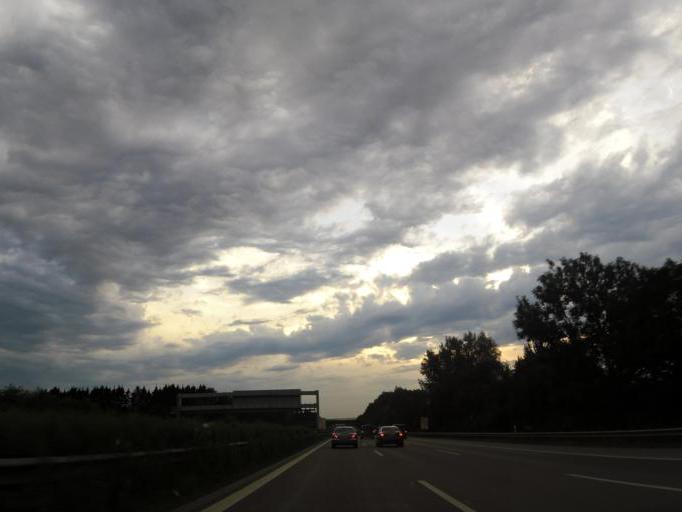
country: DE
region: Bavaria
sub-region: Upper Bavaria
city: Raubling
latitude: 47.8124
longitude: 12.0800
